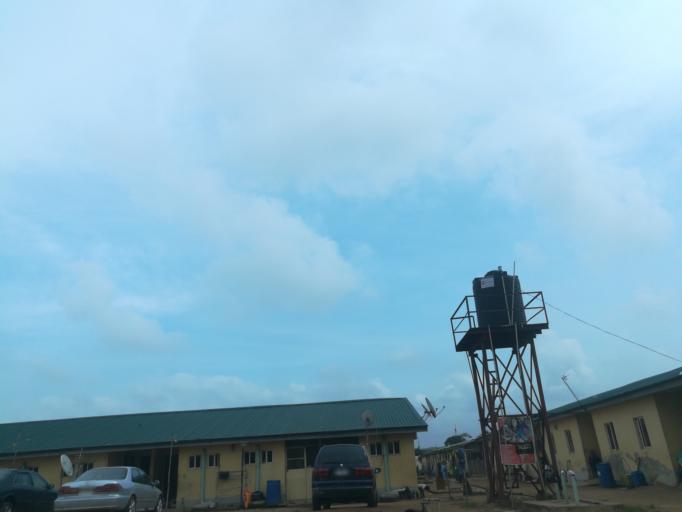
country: NG
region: Lagos
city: Oshodi
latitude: 6.5688
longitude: 3.3591
